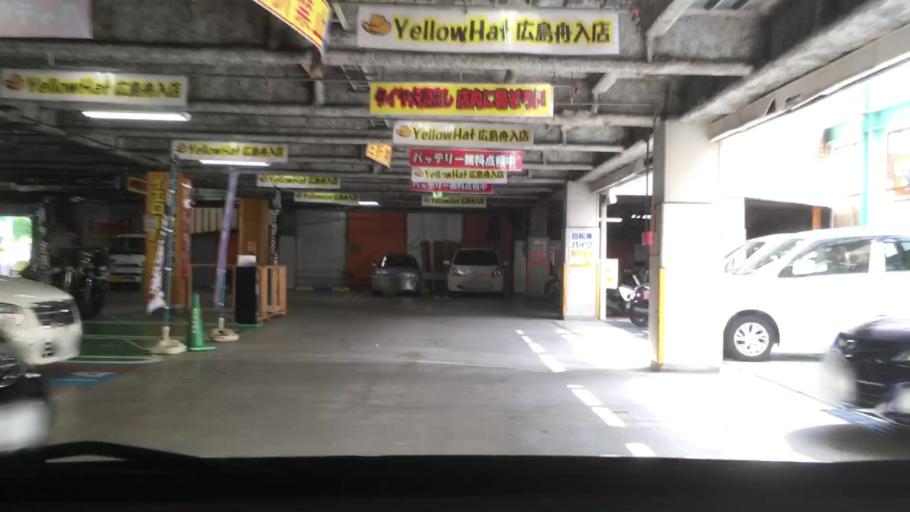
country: JP
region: Hiroshima
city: Hiroshima-shi
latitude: 34.3746
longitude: 132.4405
